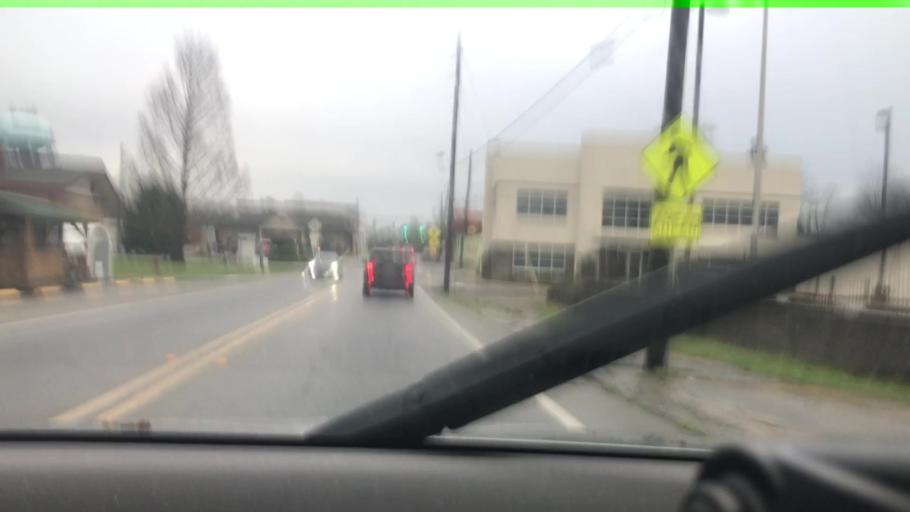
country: US
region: Georgia
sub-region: Oglethorpe County
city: Lexington
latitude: 33.8822
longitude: -83.1567
